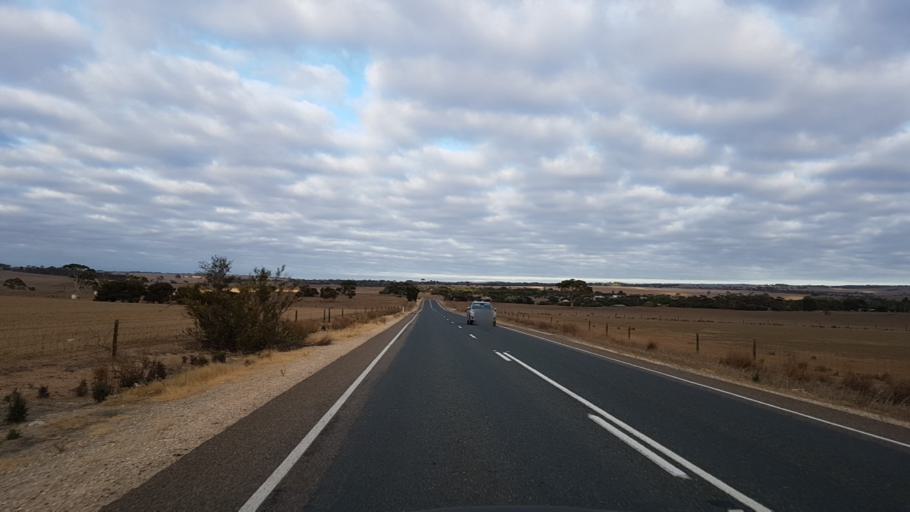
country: AU
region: South Australia
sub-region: Mount Barker
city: Callington
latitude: -35.1993
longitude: 138.9790
